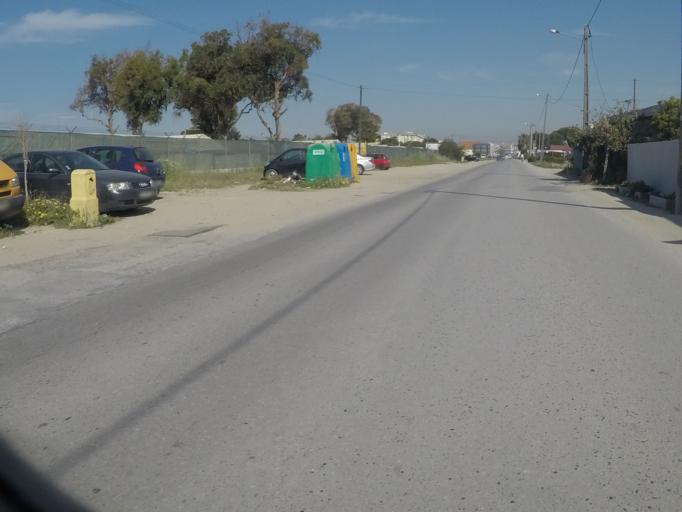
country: PT
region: Setubal
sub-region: Almada
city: Costa de Caparica
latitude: 38.6334
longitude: -9.2255
